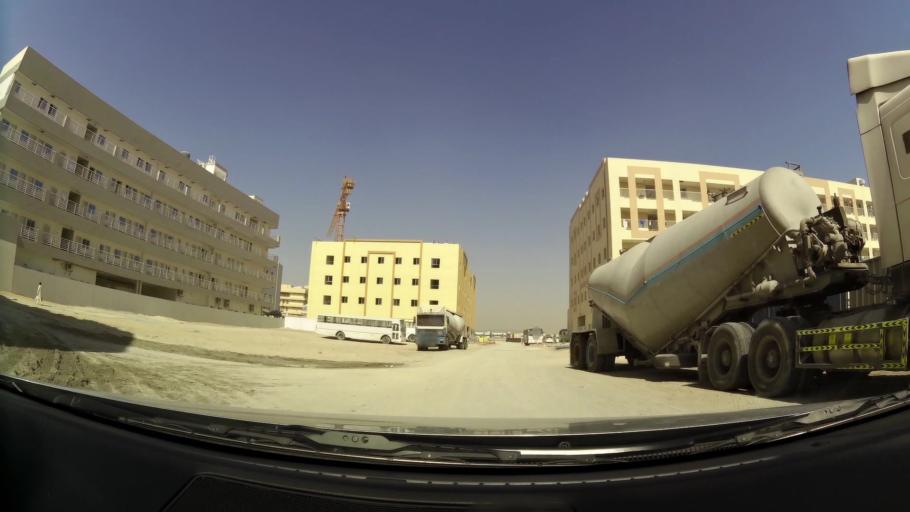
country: AE
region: Dubai
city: Dubai
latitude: 24.9929
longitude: 55.1407
